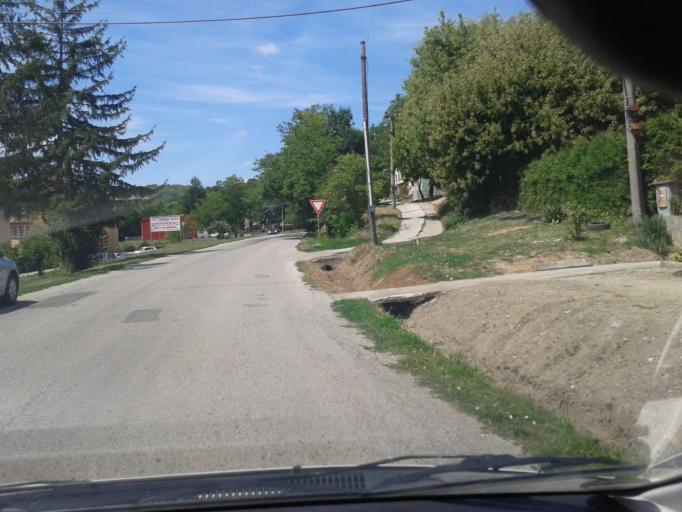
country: SK
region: Nitriansky
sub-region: Okres Nove Zamky
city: Sturovo
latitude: 47.8313
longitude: 18.7267
